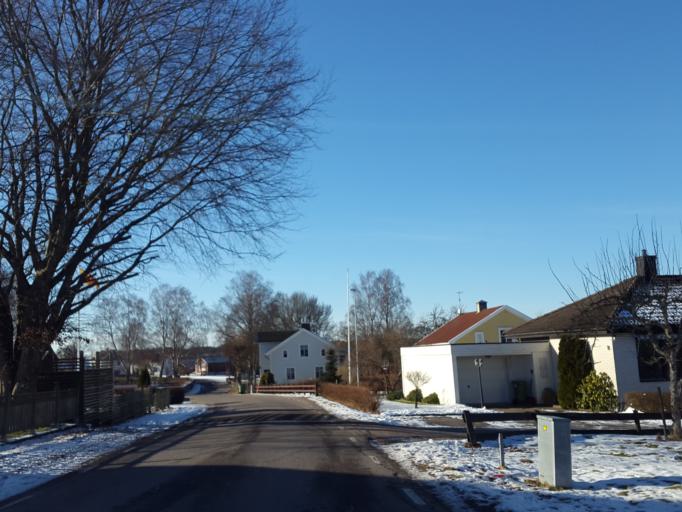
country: SE
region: Vaestra Goetaland
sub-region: Boras Kommun
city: Sandared
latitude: 57.8087
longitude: 12.7495
